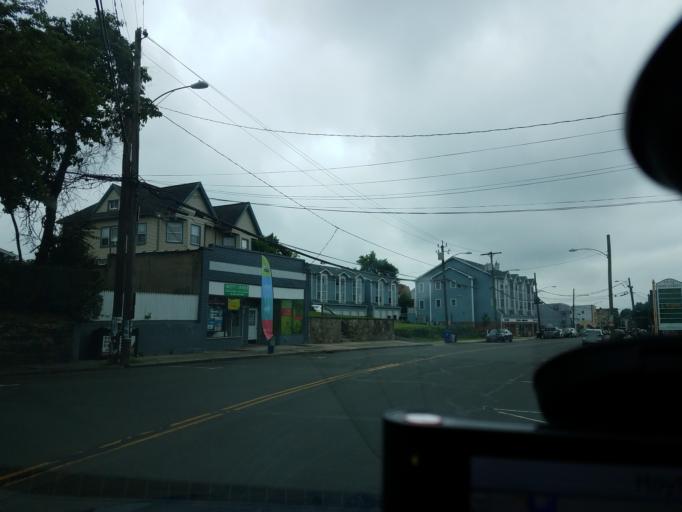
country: US
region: Connecticut
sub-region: Fairfield County
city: Norwalk
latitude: 41.1214
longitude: -73.4135
